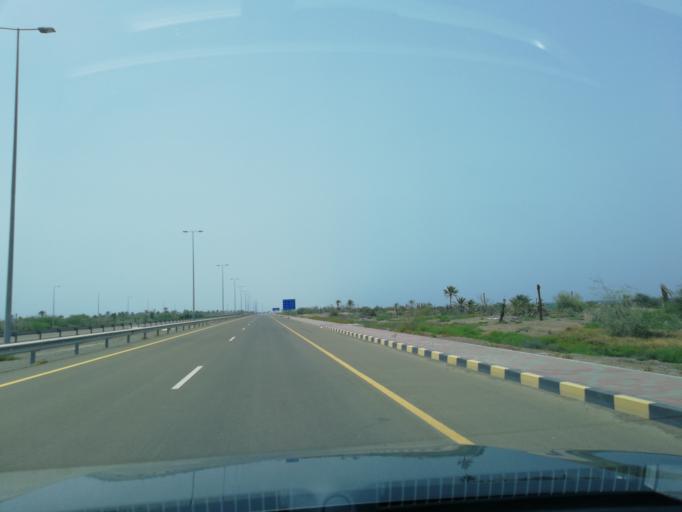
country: OM
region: Al Batinah
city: Al Liwa'
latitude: 24.6338
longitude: 56.5256
